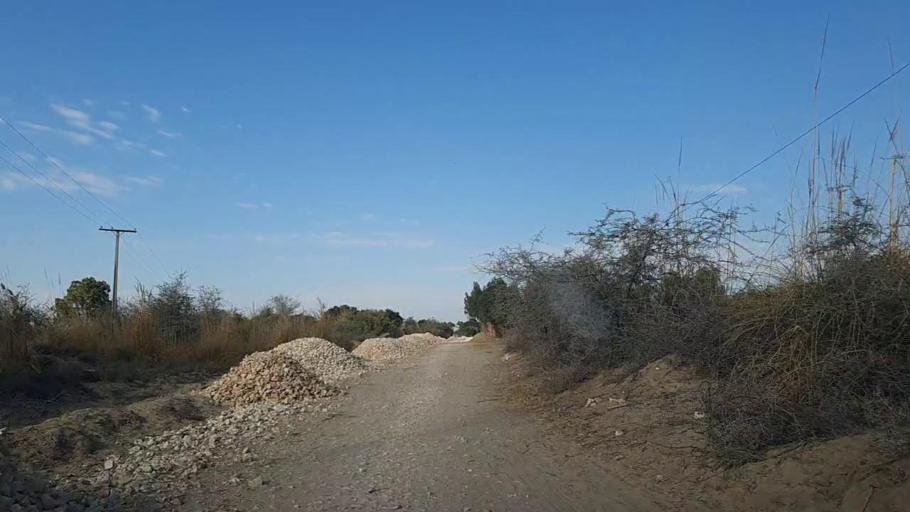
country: PK
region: Sindh
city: Jam Sahib
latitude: 26.3066
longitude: 68.8141
